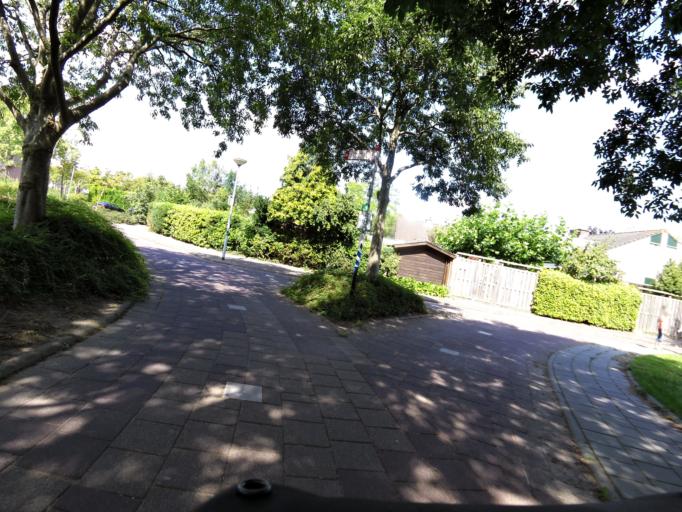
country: NL
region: South Holland
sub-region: Gemeente Barendrecht
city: Barendrecht
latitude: 51.8479
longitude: 4.5286
